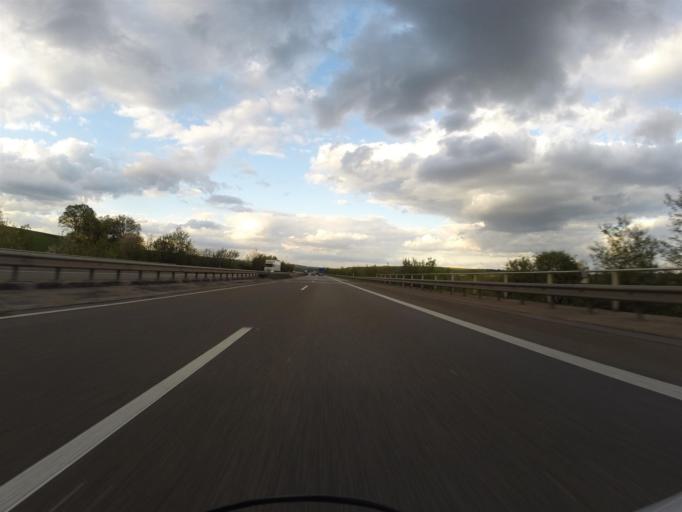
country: DE
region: Rheinland-Pfalz
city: Dreisen
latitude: 49.6125
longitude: 8.0150
